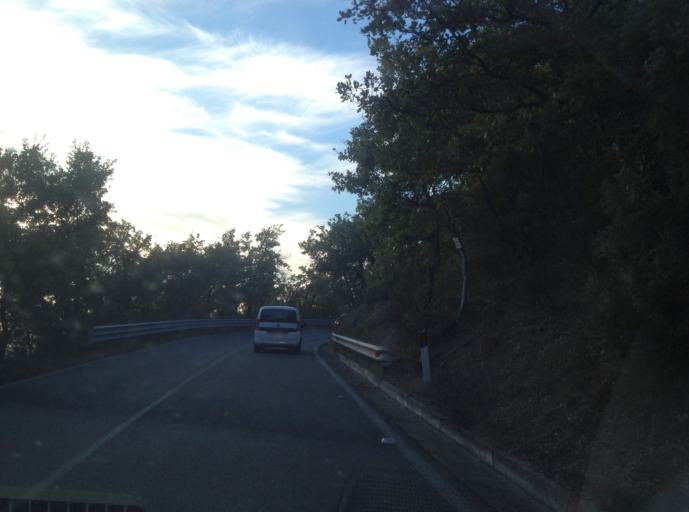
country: IT
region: Tuscany
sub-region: Provincia di Siena
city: Castellina in Chianti
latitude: 43.4284
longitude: 11.3060
